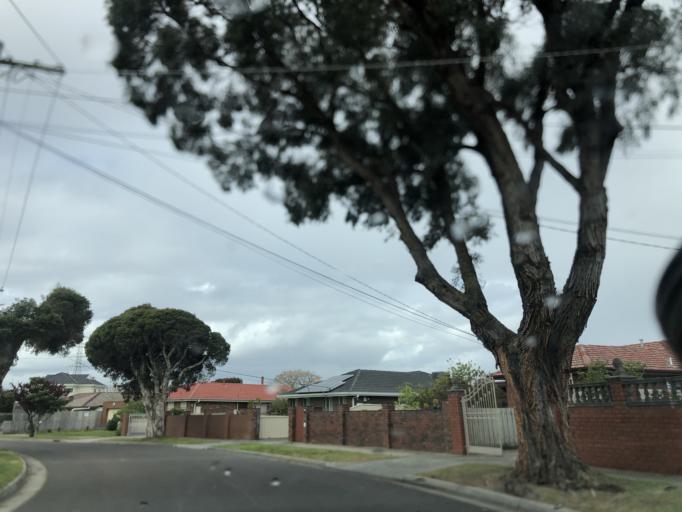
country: AU
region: Victoria
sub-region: Kingston
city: Clayton South
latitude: -37.9382
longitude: 145.1095
